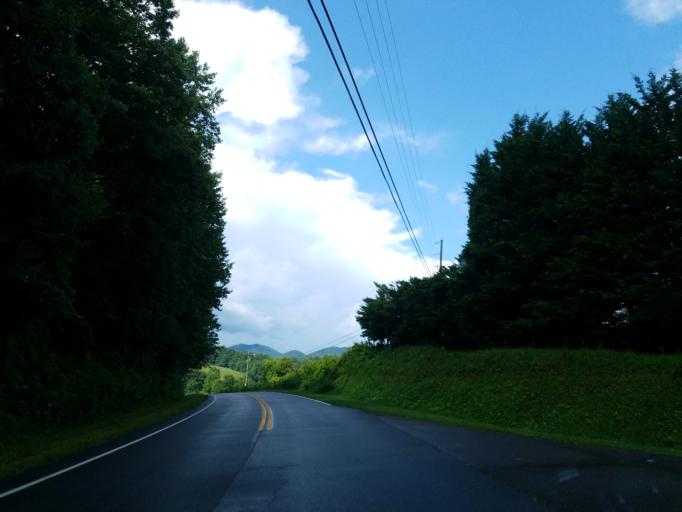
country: US
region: Georgia
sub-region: Gilmer County
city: Ellijay
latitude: 34.6816
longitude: -84.3176
